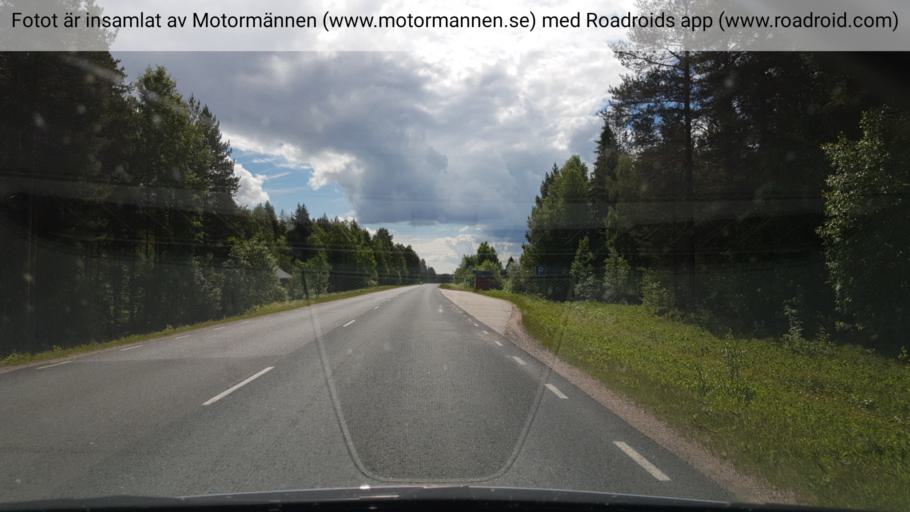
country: FI
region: Lapland
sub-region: Torniolaakso
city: Ylitornio
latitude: 66.2947
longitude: 23.6386
